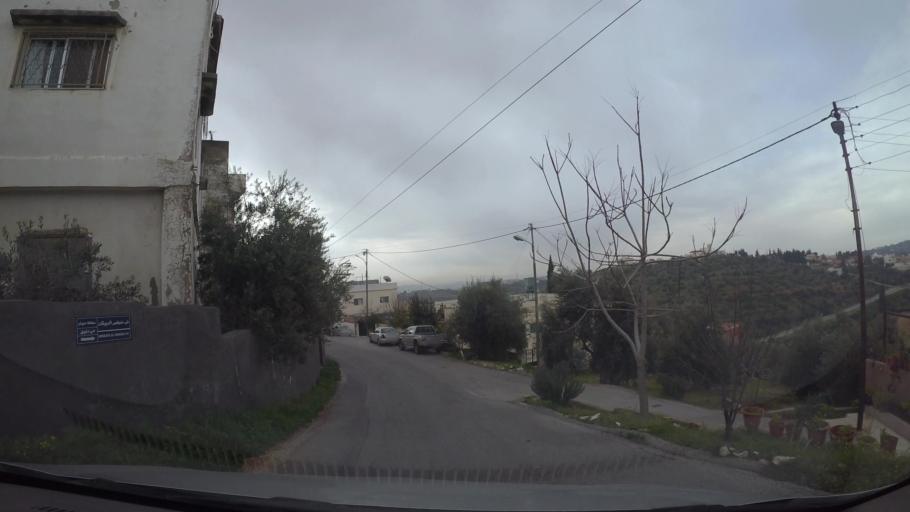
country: JO
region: Amman
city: Wadi as Sir
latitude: 31.9913
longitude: 35.8141
